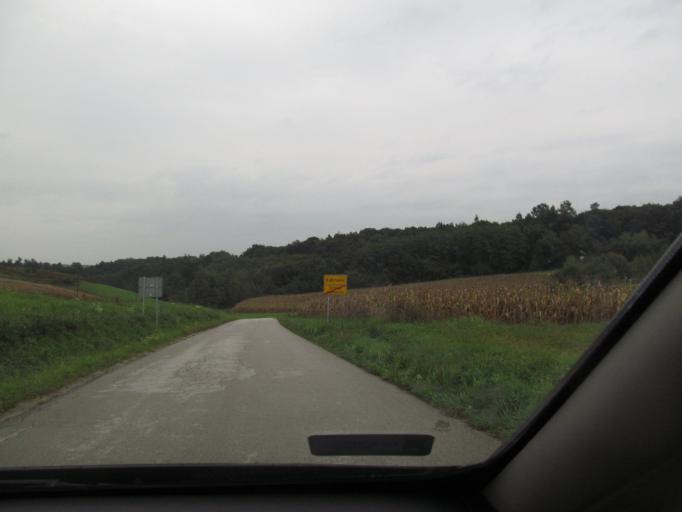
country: HR
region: Karlovacka
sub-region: Grad Karlovac
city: Karlovac
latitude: 45.4264
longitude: 15.6256
